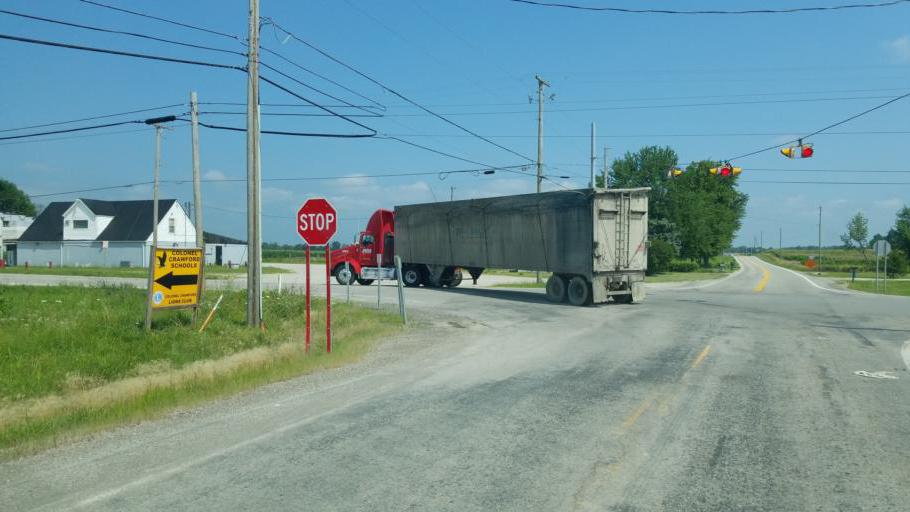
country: US
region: Ohio
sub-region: Crawford County
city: Galion
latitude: 40.8130
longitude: -82.8558
